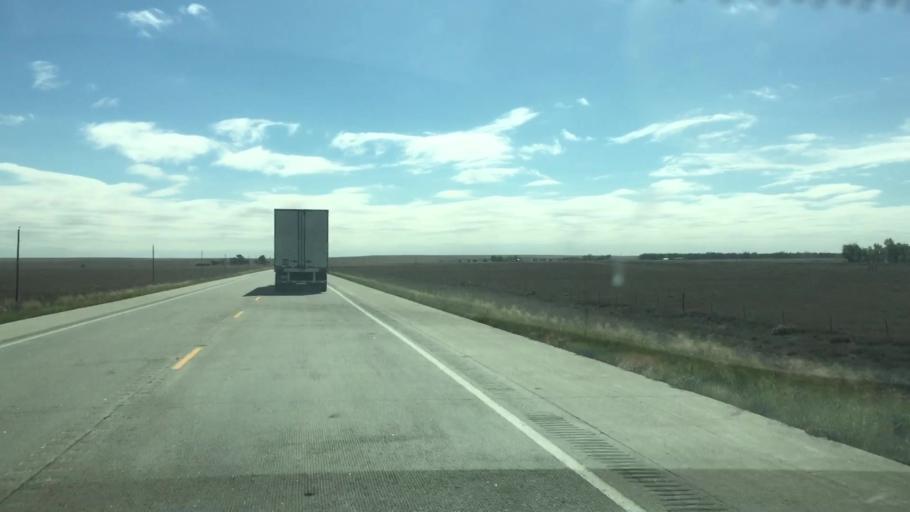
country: US
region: Colorado
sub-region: Lincoln County
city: Hugo
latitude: 39.0592
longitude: -103.3604
